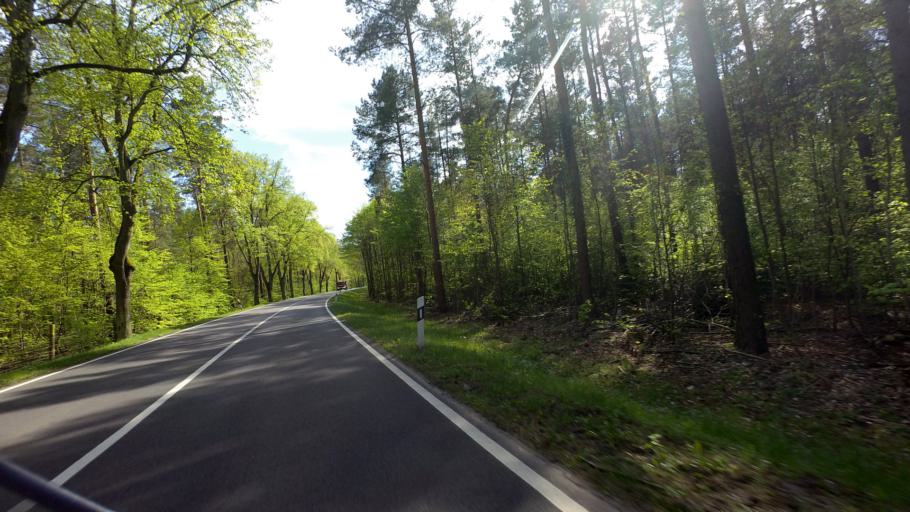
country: DE
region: Brandenburg
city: Friedrichswalde
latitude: 53.0087
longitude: 13.6006
